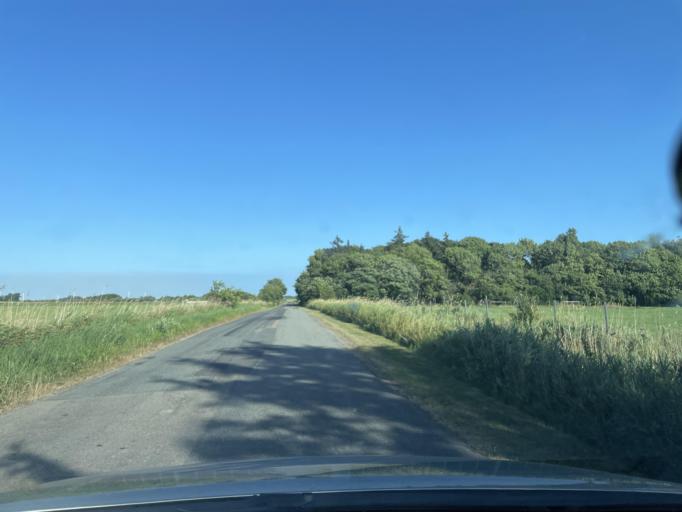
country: DE
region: Schleswig-Holstein
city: Aventoft
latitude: 54.8779
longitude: 8.8236
